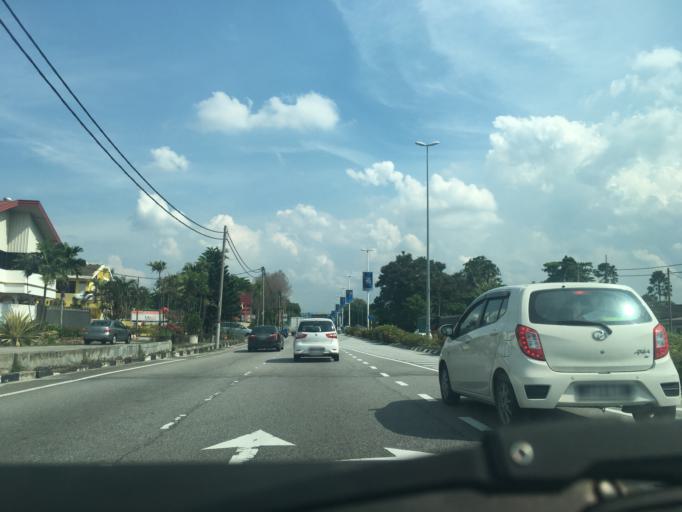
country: MY
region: Perak
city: Ipoh
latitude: 4.6169
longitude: 101.0798
